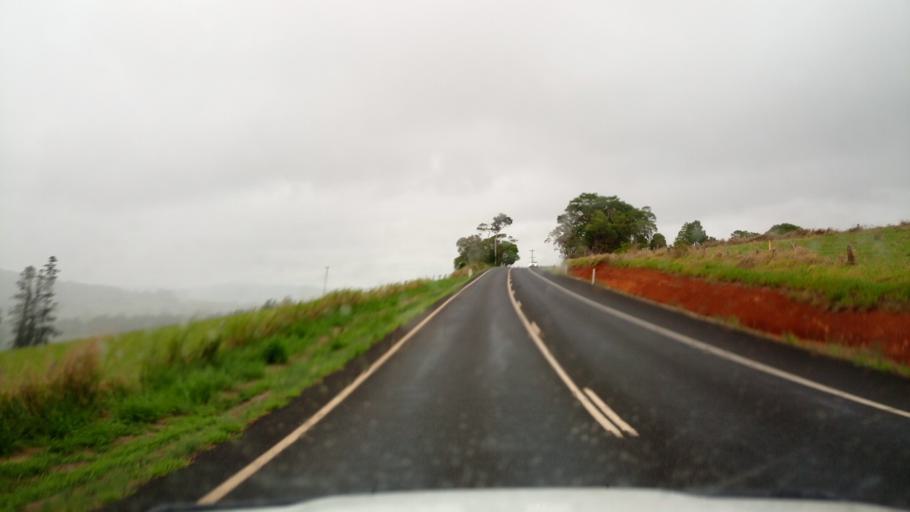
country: AU
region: Queensland
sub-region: Tablelands
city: Atherton
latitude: -17.2809
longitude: 145.5977
